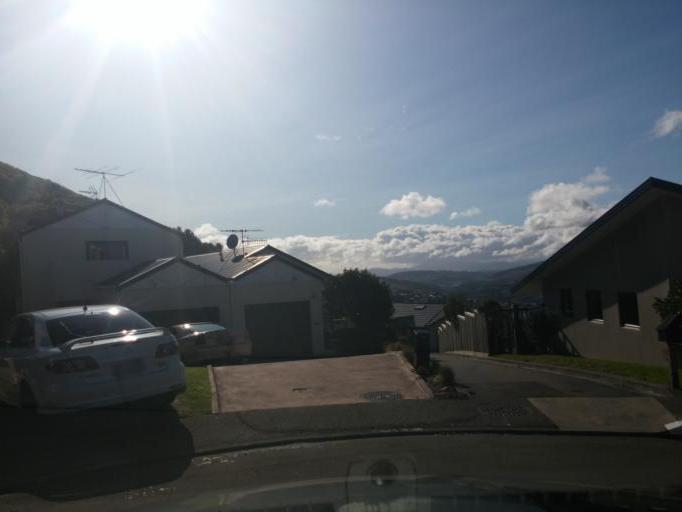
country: NZ
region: Wellington
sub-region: Wellington City
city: Wellington
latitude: -41.2330
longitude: 174.7909
